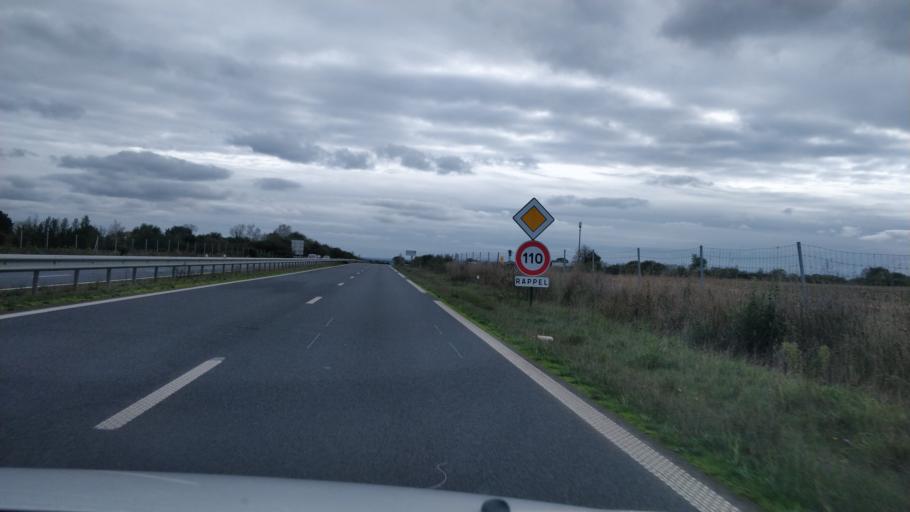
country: FR
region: Brittany
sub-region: Departement des Cotes-d'Armor
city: Plehedel
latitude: 48.7084
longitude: -3.0223
